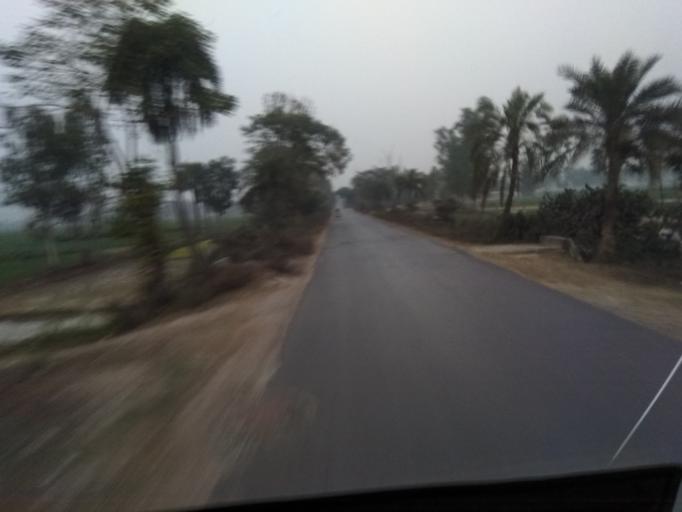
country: BD
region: Rajshahi
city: Bogra
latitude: 24.7447
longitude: 89.3369
